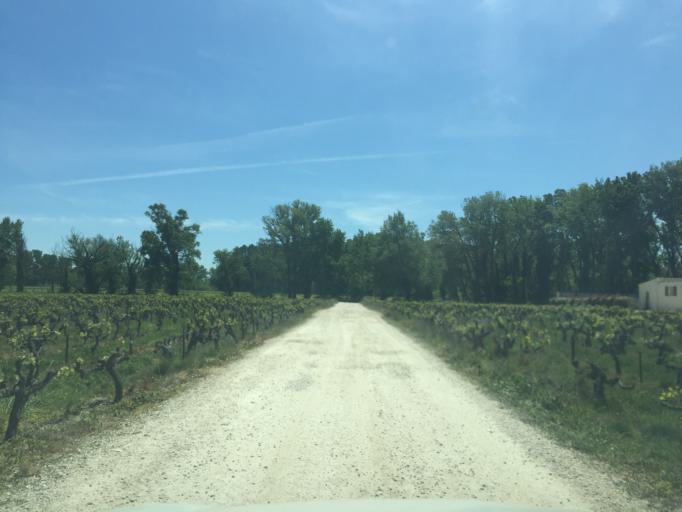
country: FR
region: Languedoc-Roussillon
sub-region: Departement du Gard
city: Roquemaure
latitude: 44.0539
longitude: 4.7982
